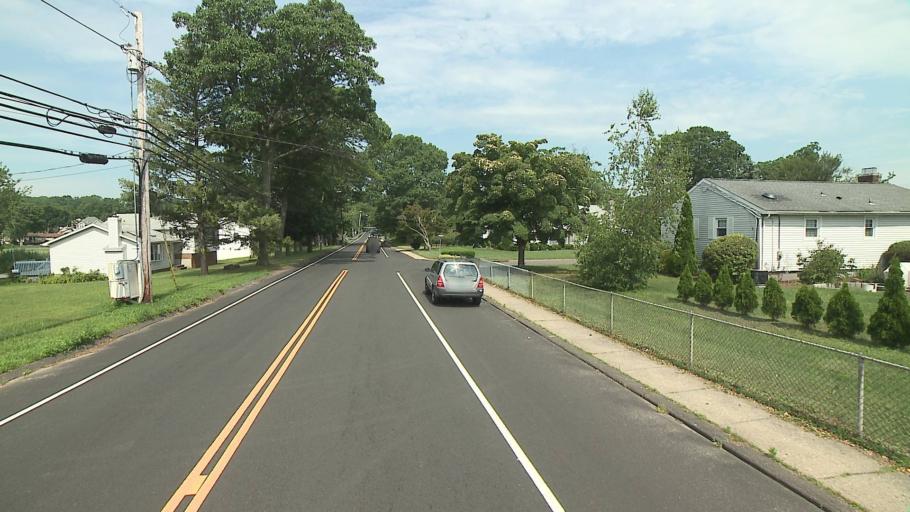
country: US
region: Connecticut
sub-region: New Haven County
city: Milford
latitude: 41.2108
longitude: -73.0266
